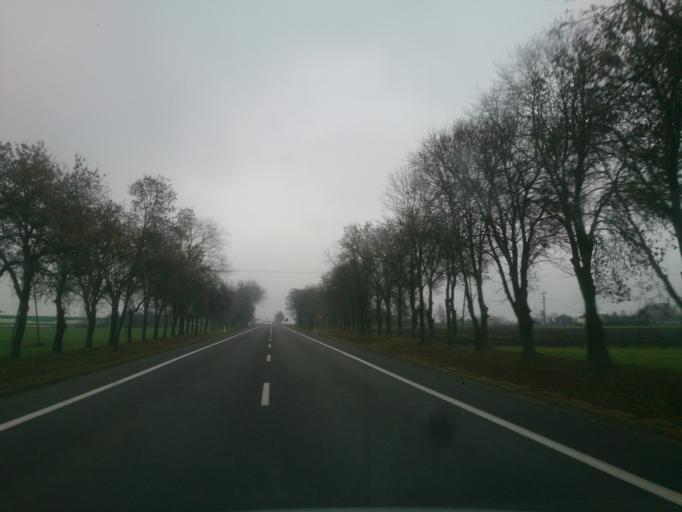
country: PL
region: Masovian Voivodeship
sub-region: Powiat plonski
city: Plonsk
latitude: 52.6036
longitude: 20.3992
